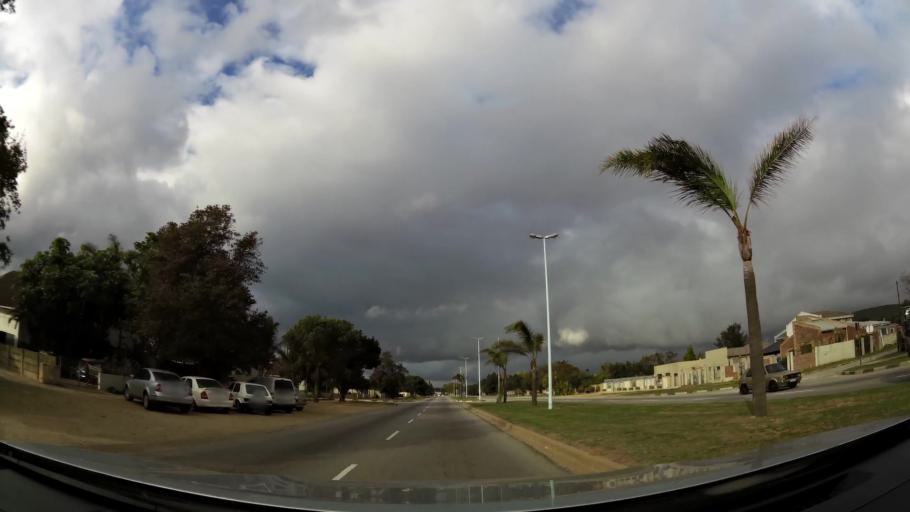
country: ZA
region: Eastern Cape
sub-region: Nelson Mandela Bay Metropolitan Municipality
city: Uitenhage
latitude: -33.8003
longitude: 25.4567
